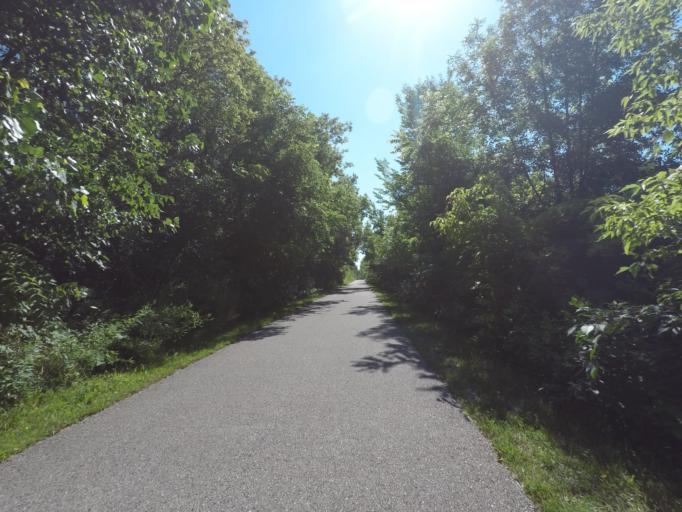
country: US
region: Wisconsin
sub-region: Milwaukee County
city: West Allis
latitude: 43.0246
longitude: -88.0043
